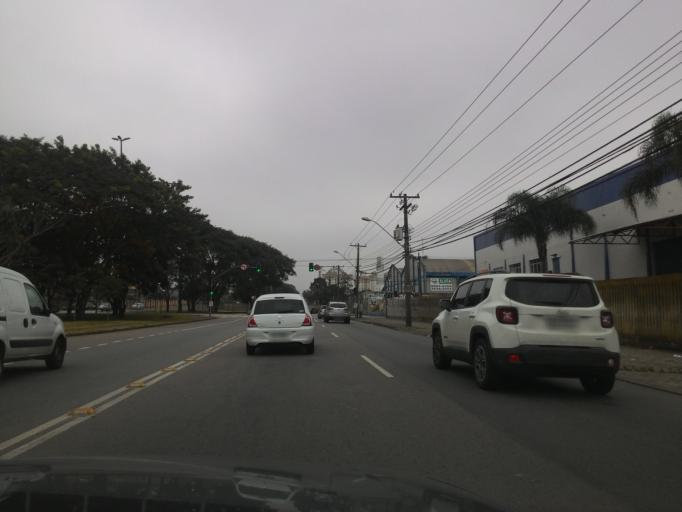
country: BR
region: Parana
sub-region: Curitiba
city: Curitiba
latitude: -25.4718
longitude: -49.2622
